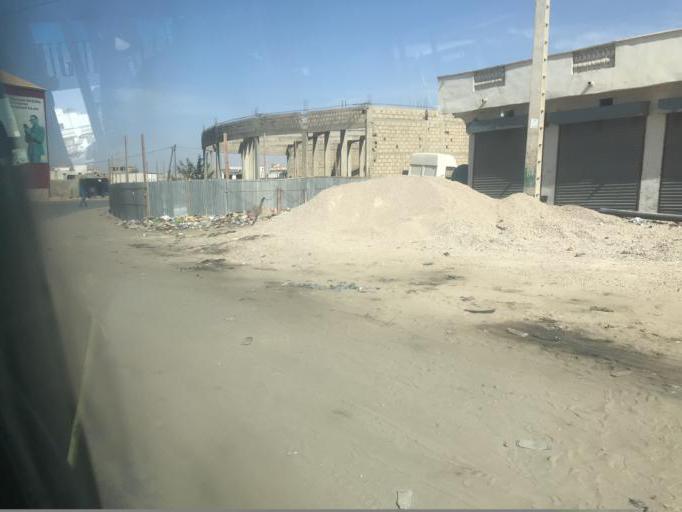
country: SN
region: Saint-Louis
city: Saint-Louis
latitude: 15.9901
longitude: -16.4866
